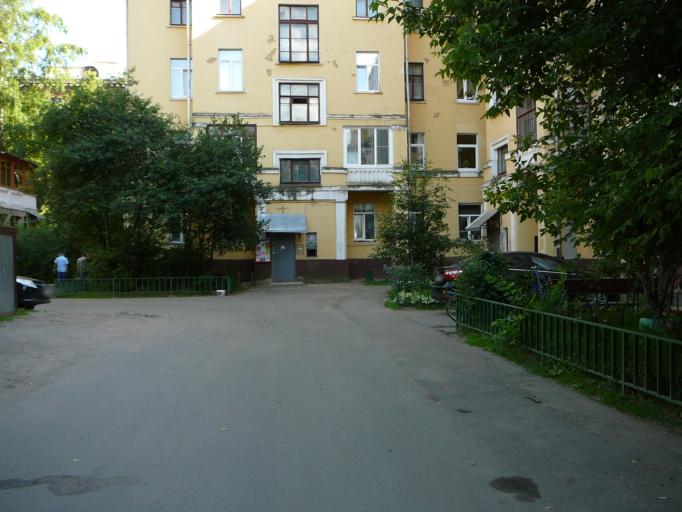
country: RU
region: Moskovskaya
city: Krasnogorsk
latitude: 55.8232
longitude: 37.3343
